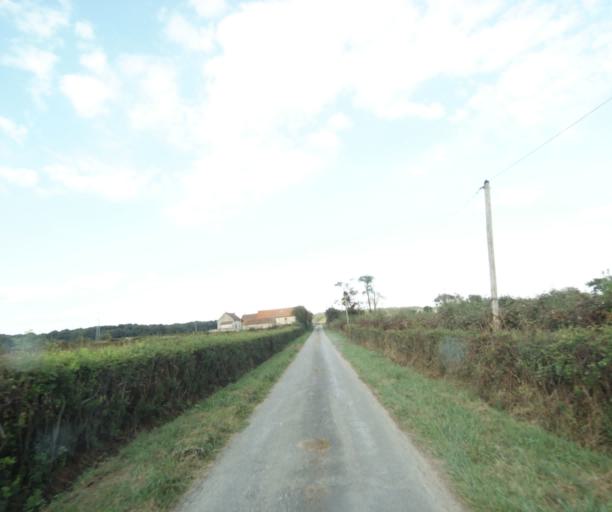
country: FR
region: Bourgogne
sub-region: Departement de Saone-et-Loire
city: Palinges
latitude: 46.5675
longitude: 4.1938
